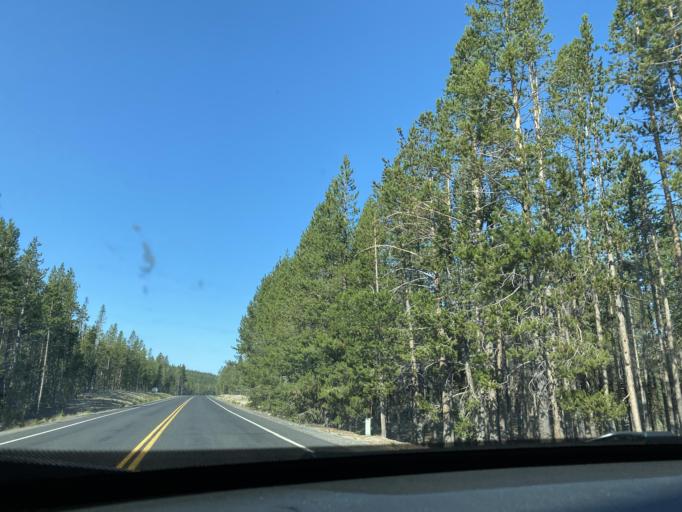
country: US
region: Oregon
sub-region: Deschutes County
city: Three Rivers
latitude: 43.7062
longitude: -121.2425
